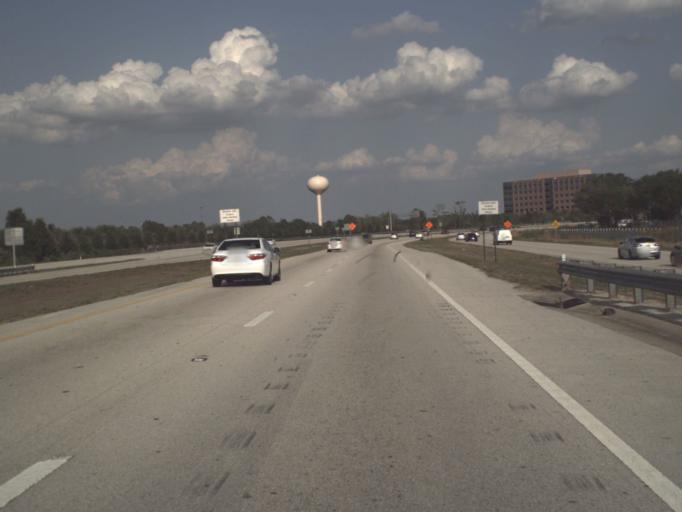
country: US
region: Florida
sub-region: Orange County
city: Lockhart
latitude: 28.6406
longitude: -81.4121
